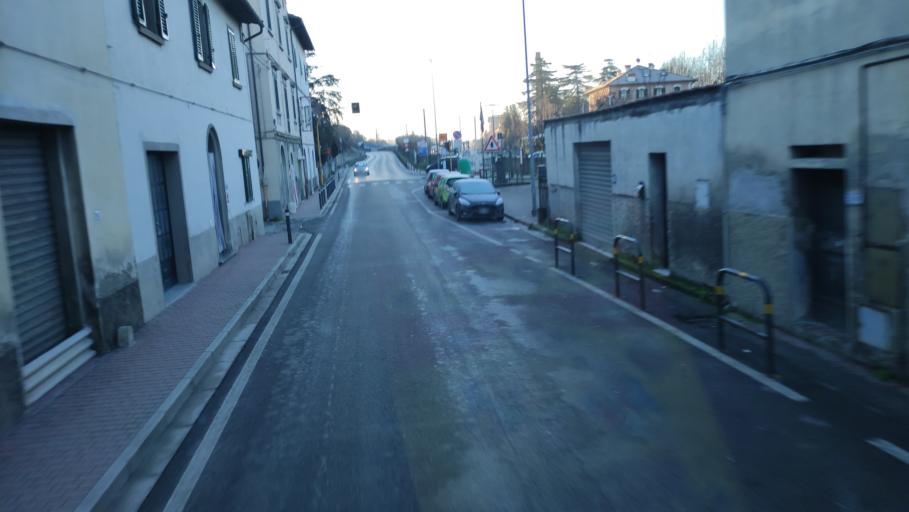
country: IT
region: Tuscany
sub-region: Province of Florence
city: Pozzale-Case Nuove
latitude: 43.6543
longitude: 10.9434
